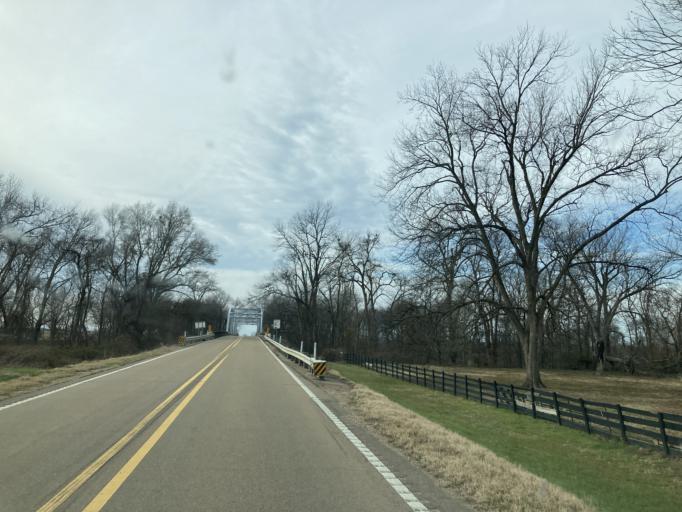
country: US
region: Mississippi
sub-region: Washington County
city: Hollandale
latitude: 33.1844
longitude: -90.6840
